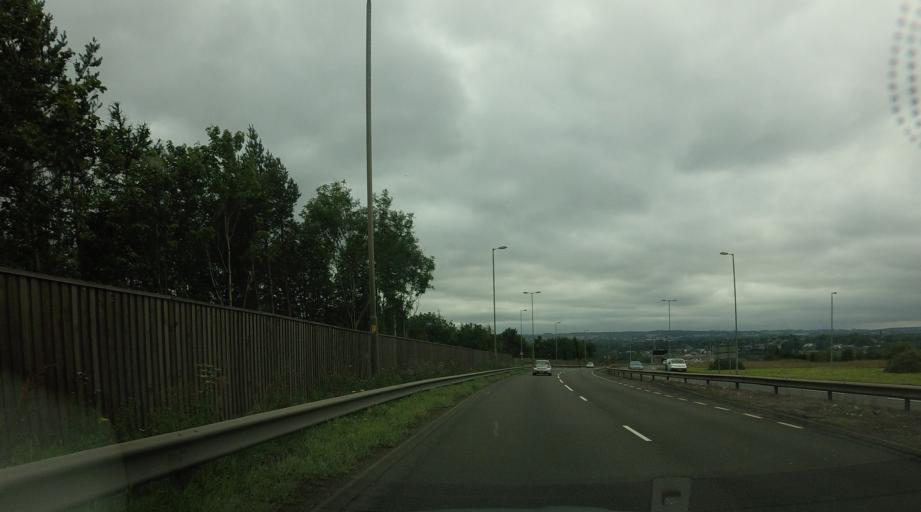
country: GB
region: Scotland
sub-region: North Lanarkshire
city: Bellshill
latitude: 55.8104
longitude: -4.0387
